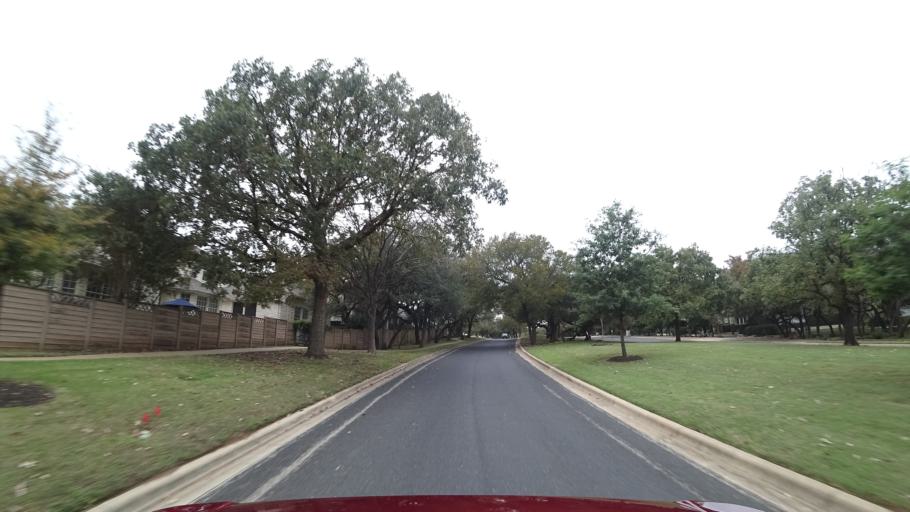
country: US
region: Texas
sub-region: Williamson County
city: Anderson Mill
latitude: 30.4416
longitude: -97.8293
